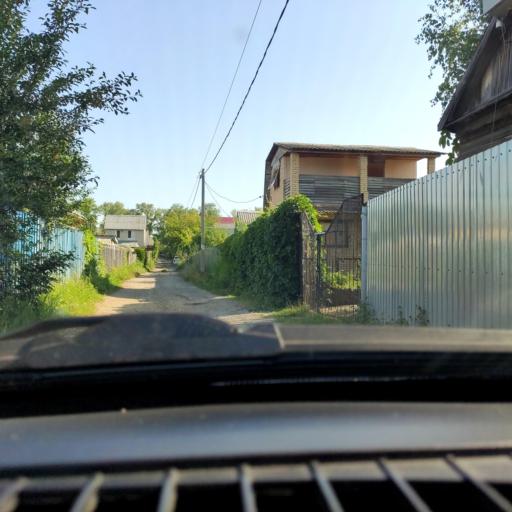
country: RU
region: Samara
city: Zhigulevsk
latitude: 53.4543
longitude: 49.5446
